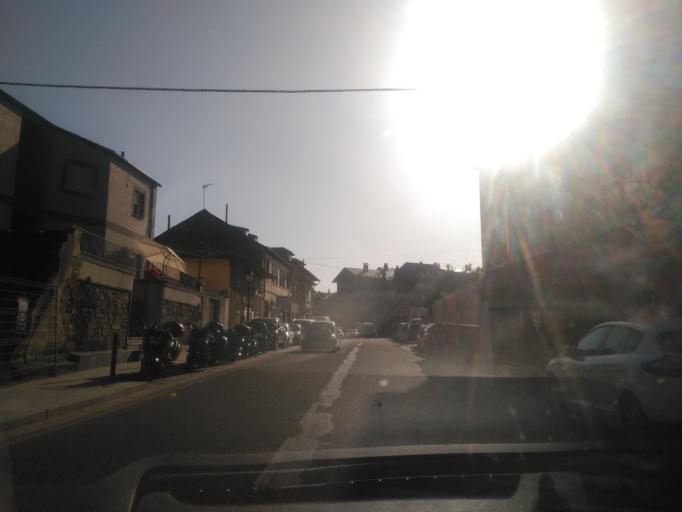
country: ES
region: Castille and Leon
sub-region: Provincia de Zamora
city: Puebla de Sanabria
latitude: 42.0515
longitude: -6.6340
